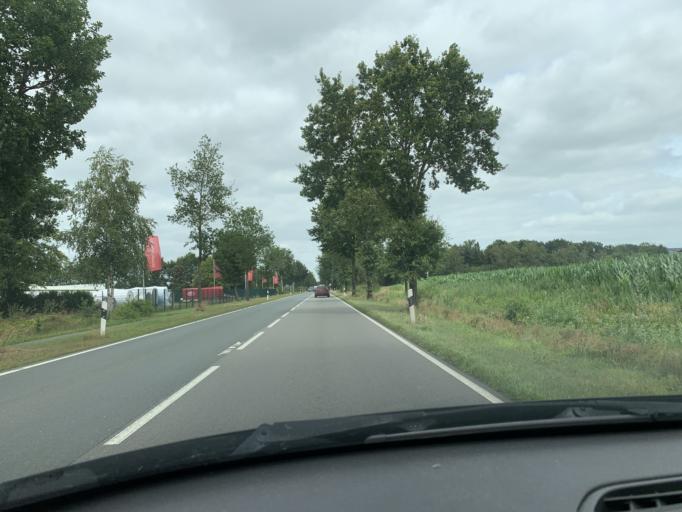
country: DE
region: Lower Saxony
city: Westerstede
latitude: 53.2676
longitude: 7.9478
